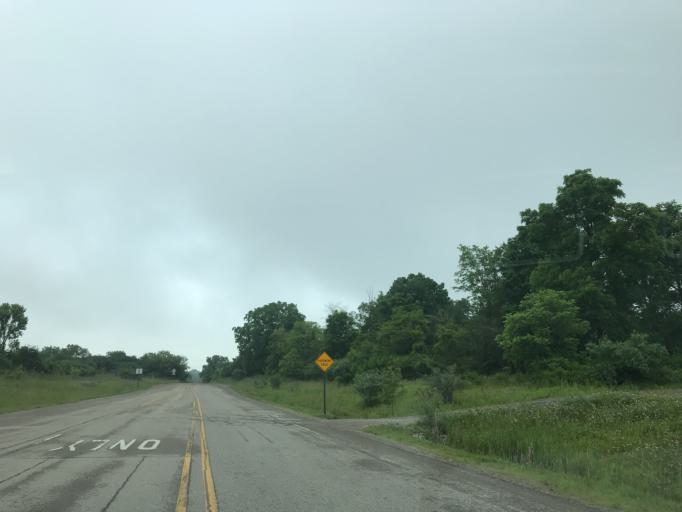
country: US
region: Michigan
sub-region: Washtenaw County
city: Ypsilanti
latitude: 42.2751
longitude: -83.6231
